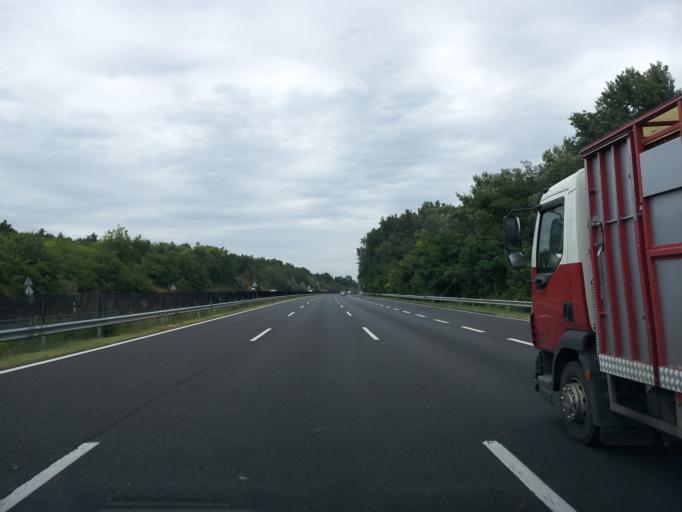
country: HU
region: Fejer
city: Baracska
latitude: 47.3080
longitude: 18.7457
